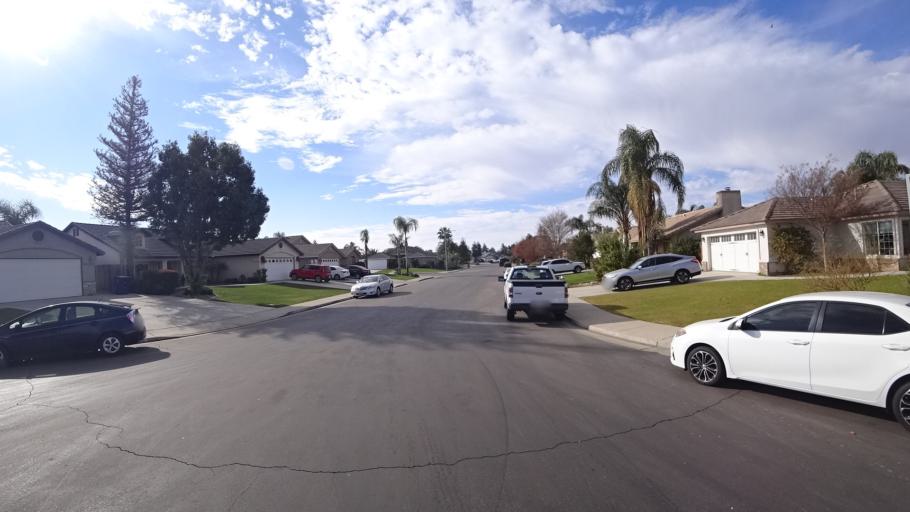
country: US
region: California
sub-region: Kern County
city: Greenacres
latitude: 35.3994
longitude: -119.1225
